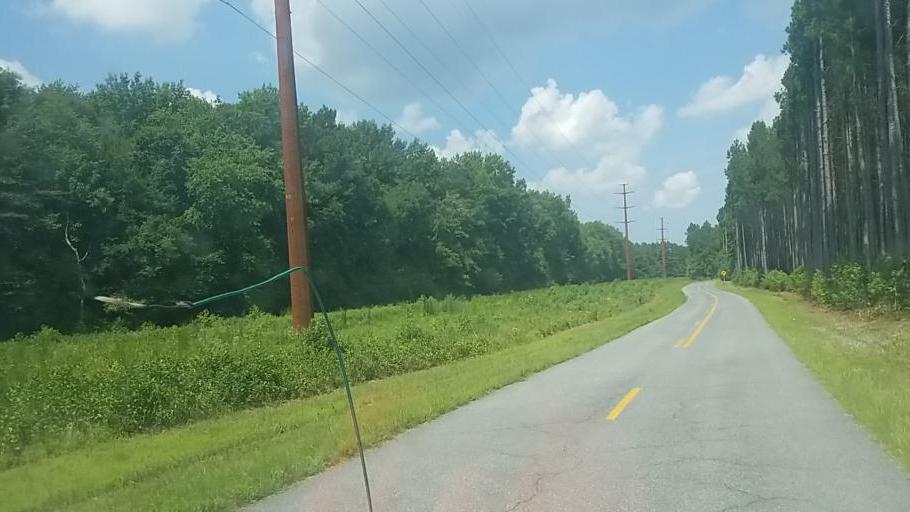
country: US
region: Maryland
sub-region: Worcester County
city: Snow Hill
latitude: 38.2660
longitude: -75.4683
